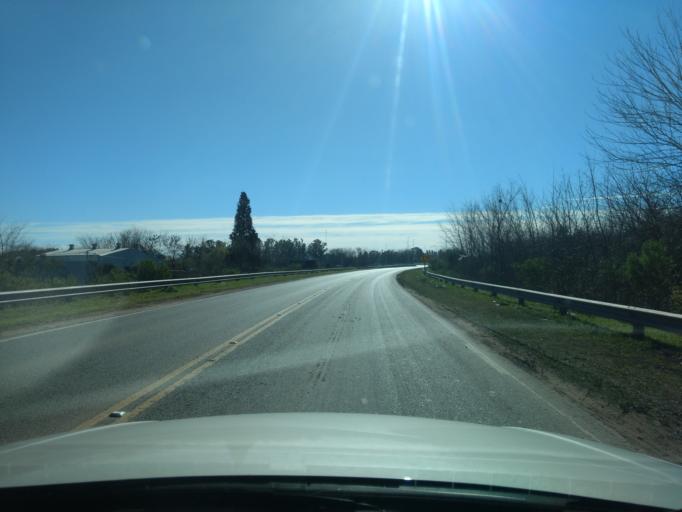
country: AR
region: Buenos Aires
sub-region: Partido de Lujan
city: Lujan
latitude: -34.5943
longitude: -59.1058
